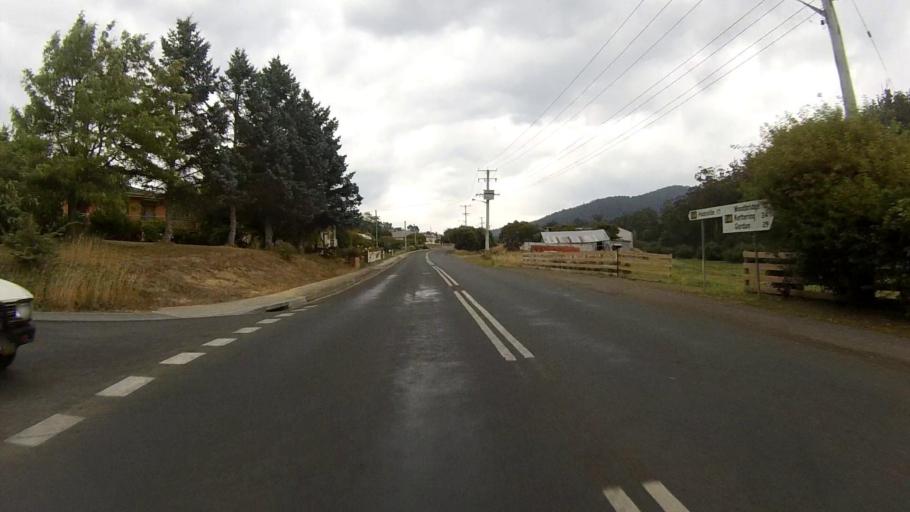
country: AU
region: Tasmania
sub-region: Huon Valley
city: Cygnet
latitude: -43.1533
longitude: 147.0722
